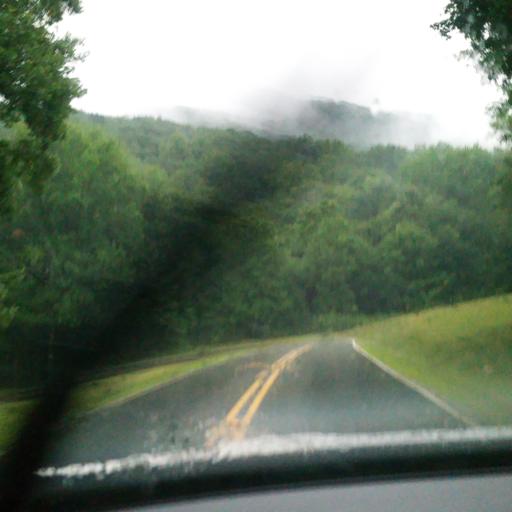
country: US
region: North Carolina
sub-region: Yancey County
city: Burnsville
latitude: 35.8177
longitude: -82.3460
